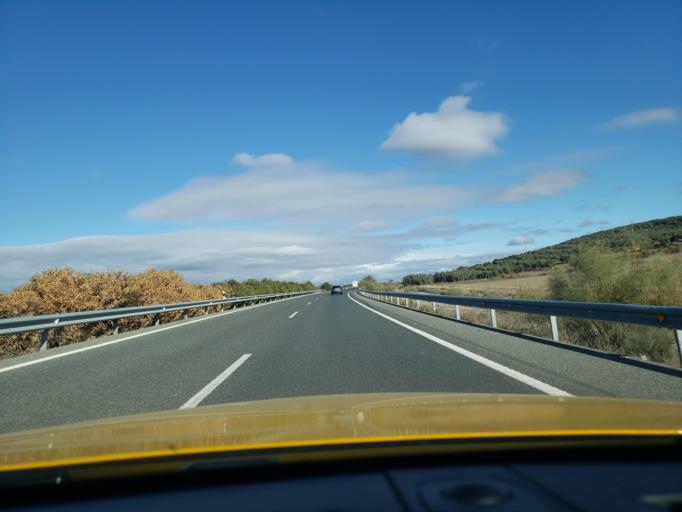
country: ES
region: Andalusia
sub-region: Provincia de Malaga
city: Archidona
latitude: 37.1004
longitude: -4.3148
